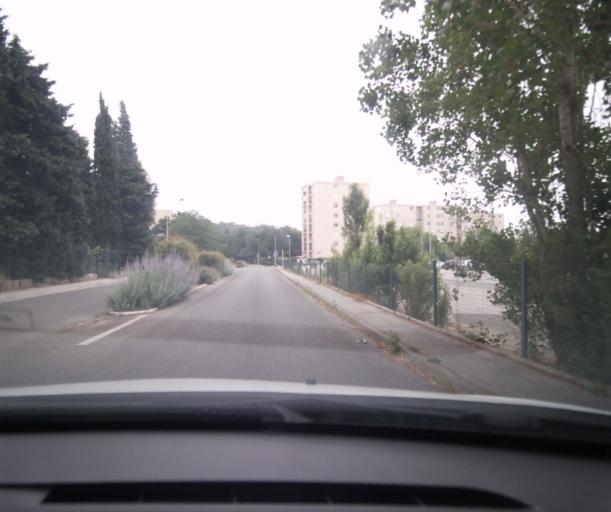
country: FR
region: Provence-Alpes-Cote d'Azur
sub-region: Departement du Var
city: La Valette-du-Var
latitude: 43.1282
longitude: 5.9860
